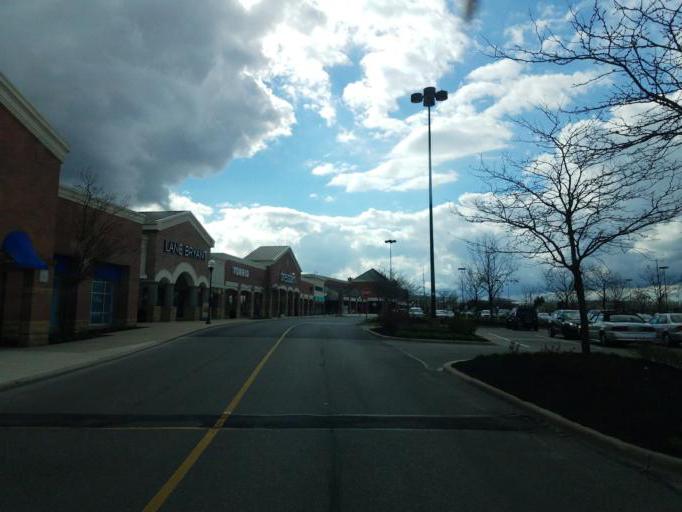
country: US
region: Ohio
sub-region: Franklin County
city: Worthington
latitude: 40.1403
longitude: -82.9881
